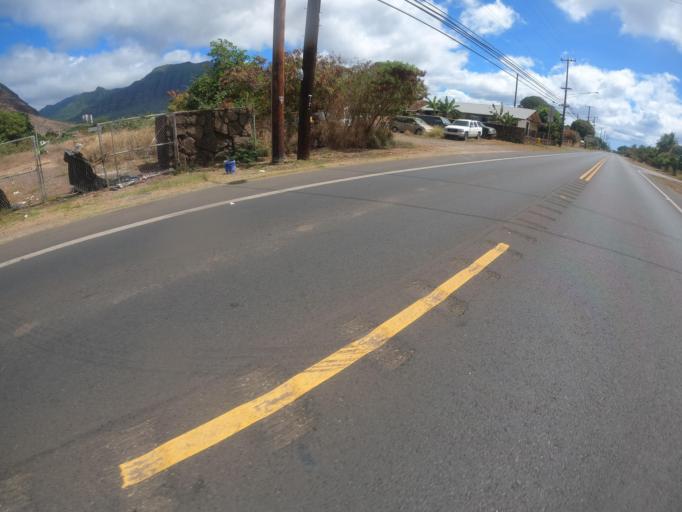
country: US
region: Hawaii
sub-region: Honolulu County
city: Makaha
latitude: 21.4749
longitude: -158.2180
